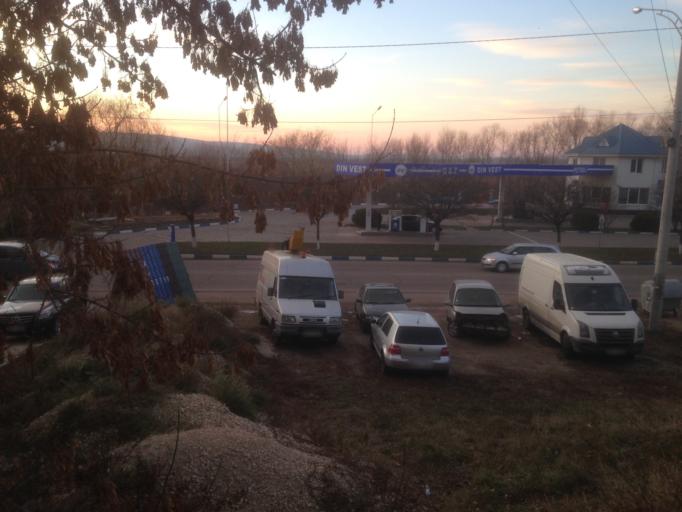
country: MD
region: Orhei
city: Orhei
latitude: 47.3751
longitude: 28.8176
